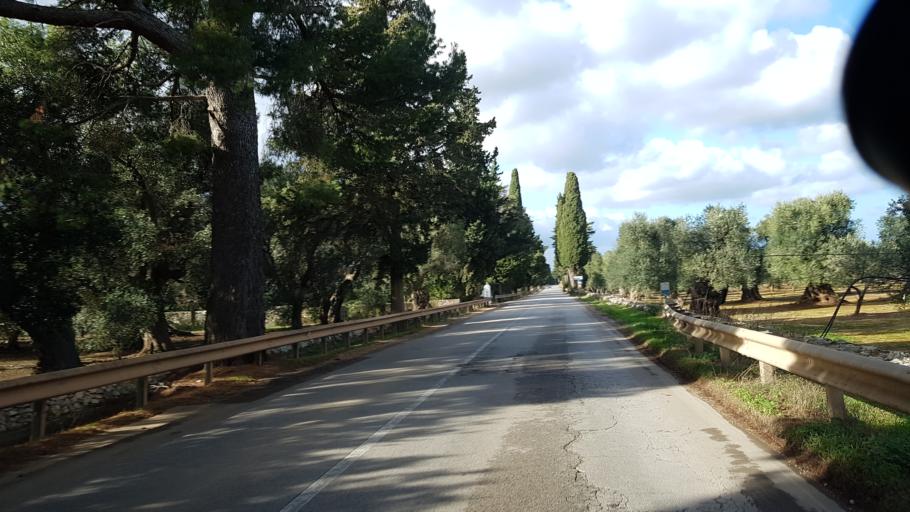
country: IT
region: Apulia
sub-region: Provincia di Brindisi
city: Montalbano
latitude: 40.7585
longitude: 17.5334
